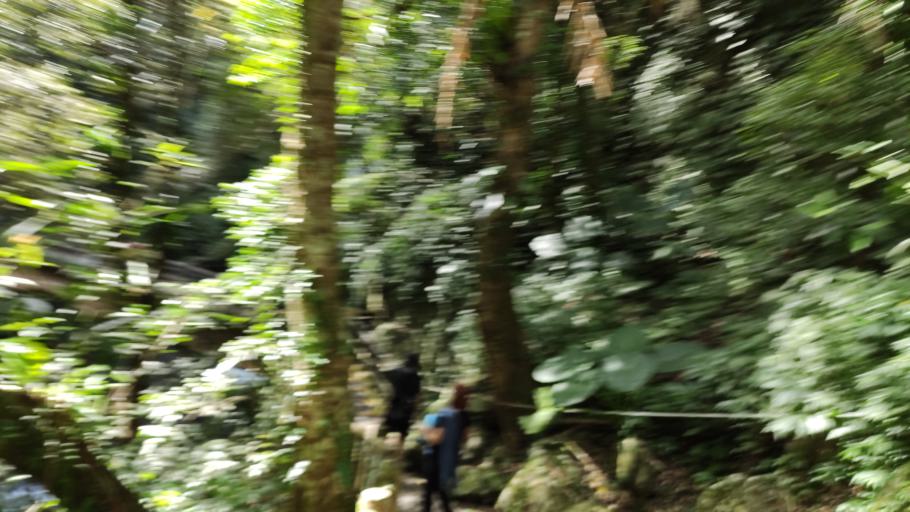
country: TW
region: Taiwan
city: Daxi
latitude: 24.8180
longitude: 121.4501
